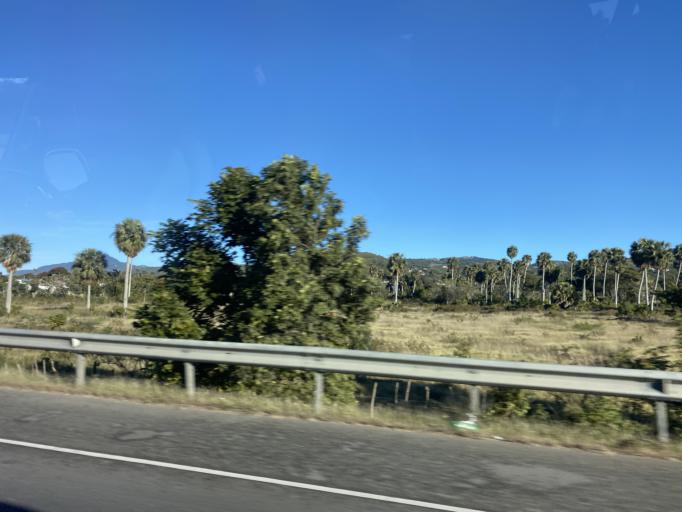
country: DO
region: Santiago
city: Tamboril
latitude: 19.4924
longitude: -70.6468
